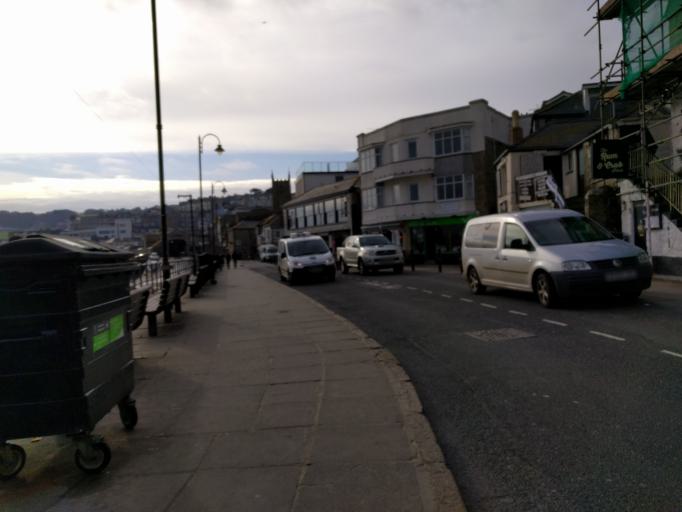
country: GB
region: England
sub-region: Cornwall
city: St Ives
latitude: 50.2144
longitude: -5.4799
